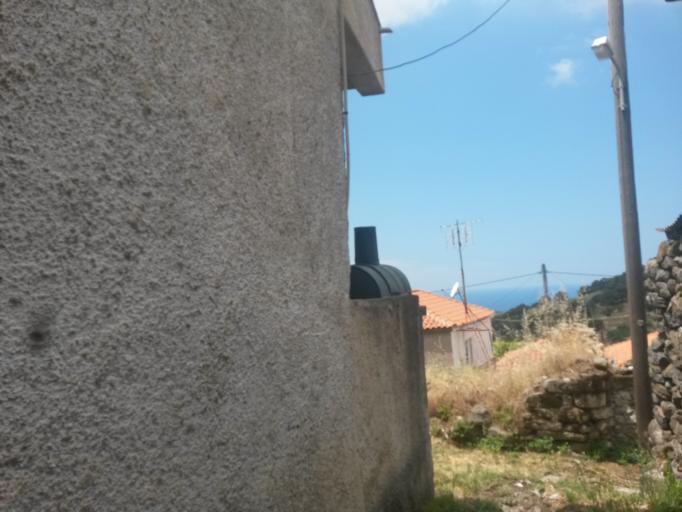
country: GR
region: North Aegean
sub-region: Nomos Lesvou
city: Petra
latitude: 39.2617
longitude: 26.0753
